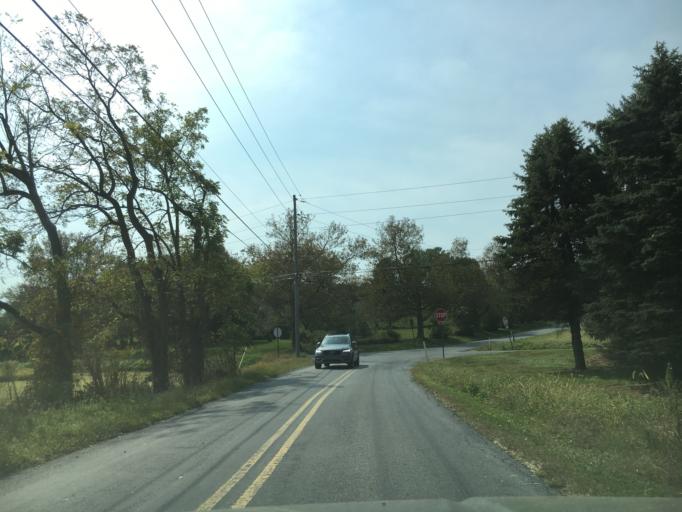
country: US
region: Pennsylvania
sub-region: Berks County
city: Topton
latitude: 40.5524
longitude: -75.7089
